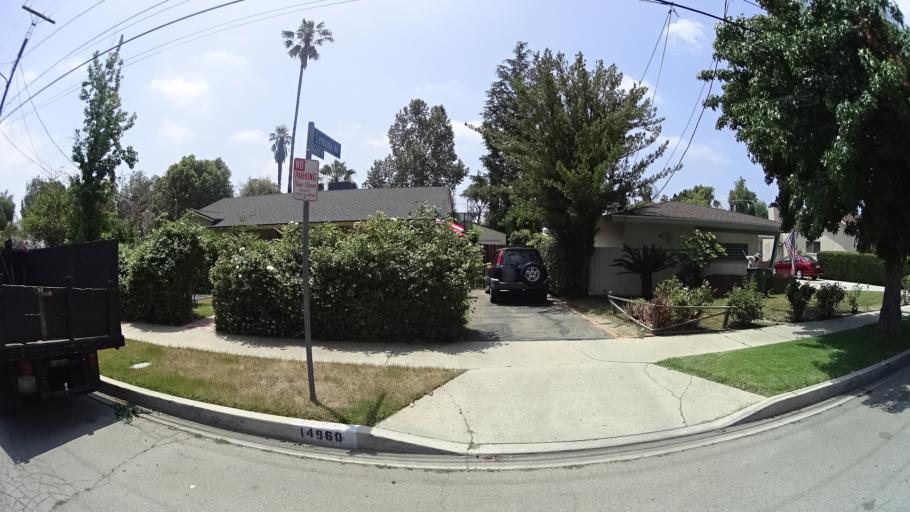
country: US
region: California
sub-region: Los Angeles County
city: Van Nuys
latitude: 34.1903
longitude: -118.4598
